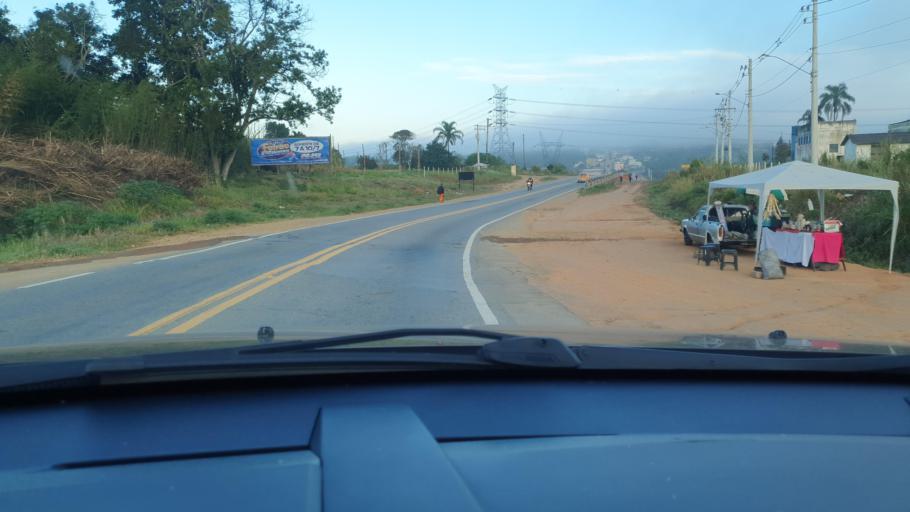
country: BR
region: Sao Paulo
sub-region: Vargem Grande Paulista
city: Vargem Grande Paulista
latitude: -23.6569
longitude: -47.0787
